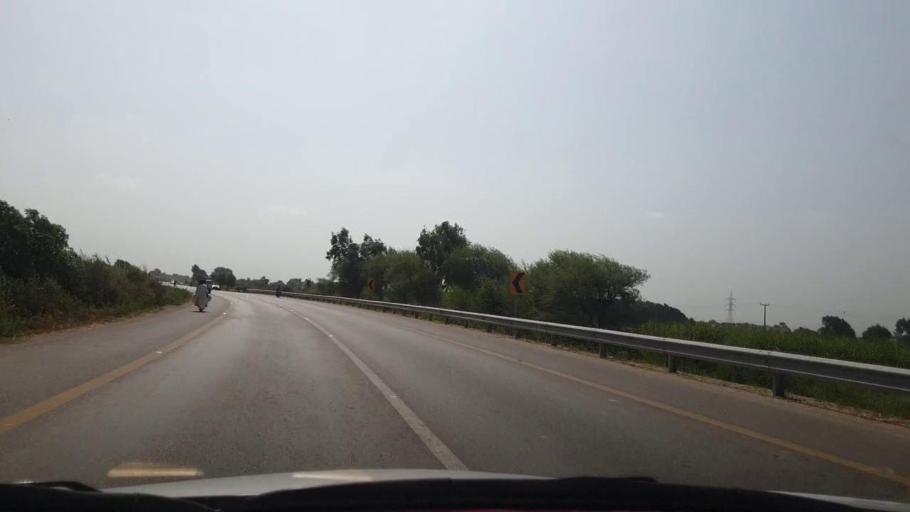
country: PK
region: Sindh
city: Matli
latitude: 25.0710
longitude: 68.6225
